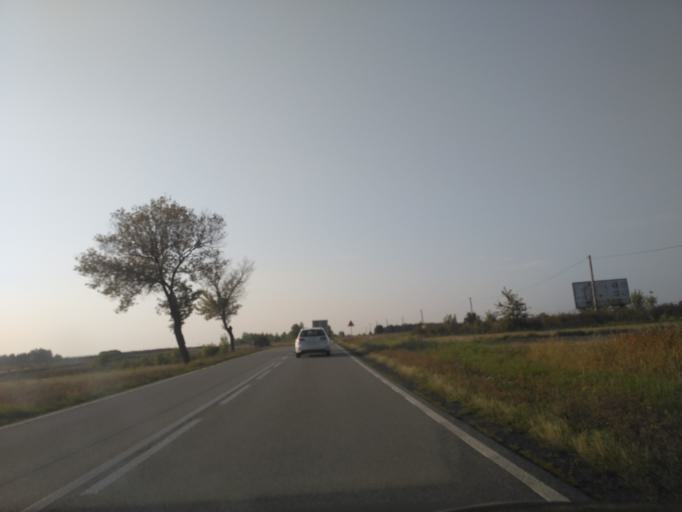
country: PL
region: Lublin Voivodeship
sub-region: Powiat janowski
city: Modliborzyce
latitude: 50.7860
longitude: 22.3208
